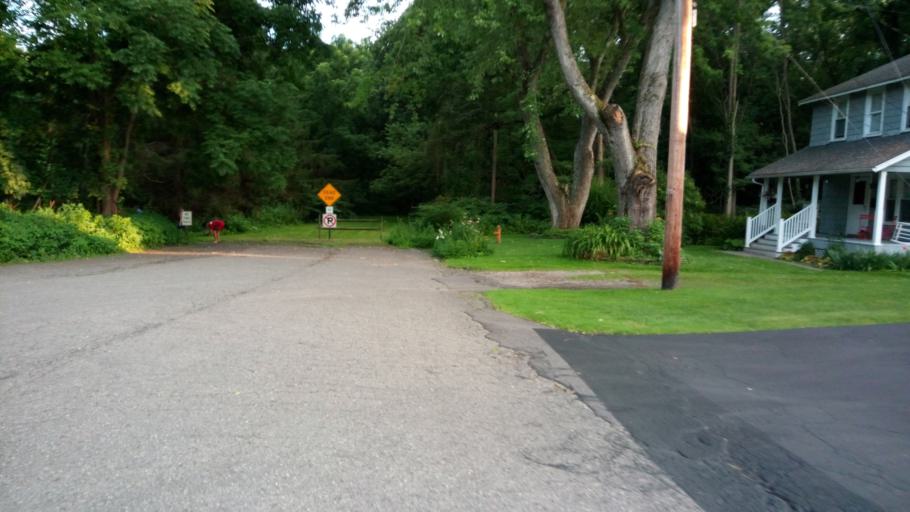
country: US
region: New York
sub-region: Chemung County
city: West Elmira
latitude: 42.0754
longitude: -76.8484
